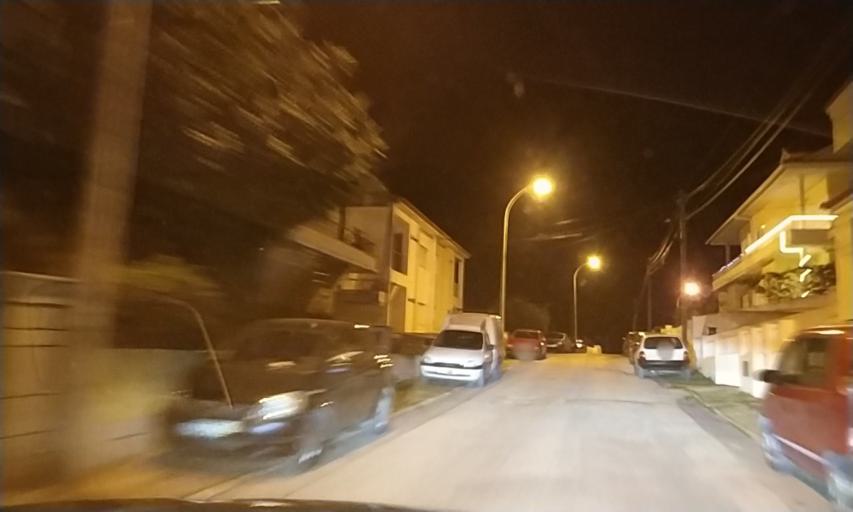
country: PT
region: Setubal
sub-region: Setubal
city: Setubal
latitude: 38.5291
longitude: -8.9050
